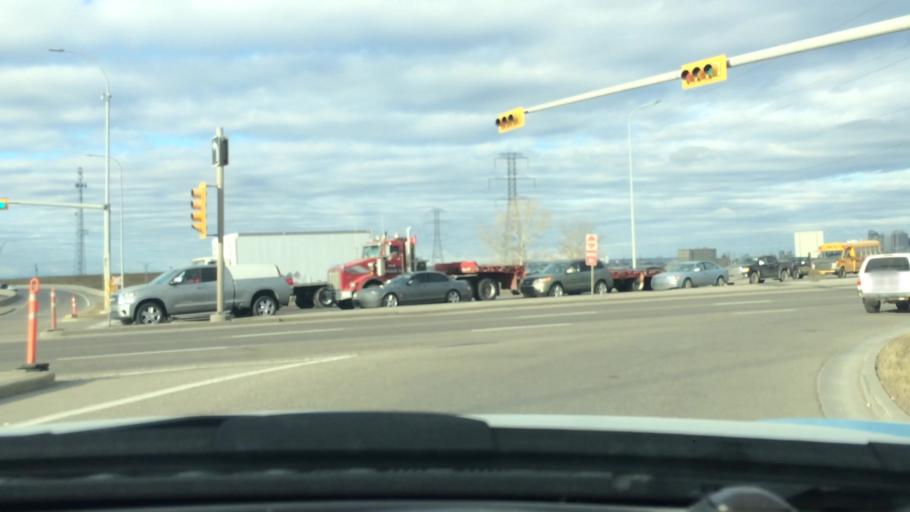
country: CA
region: Alberta
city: Calgary
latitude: 51.0155
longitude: -114.0021
